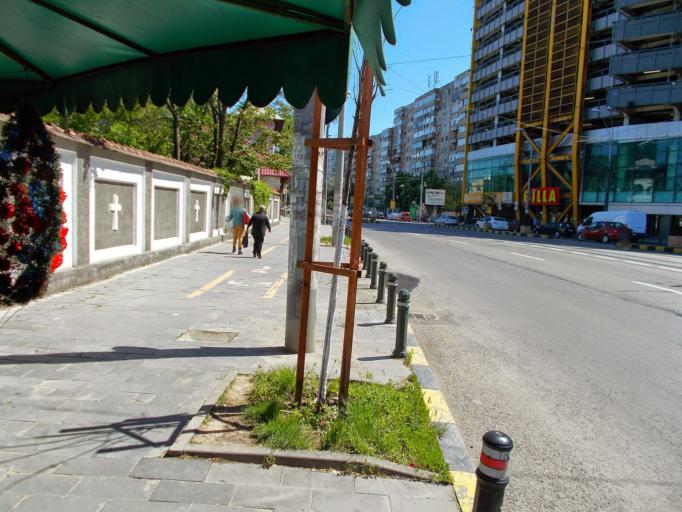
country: RO
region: Bucuresti
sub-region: Municipiul Bucuresti
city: Bucuresti
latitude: 44.4017
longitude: 26.0989
